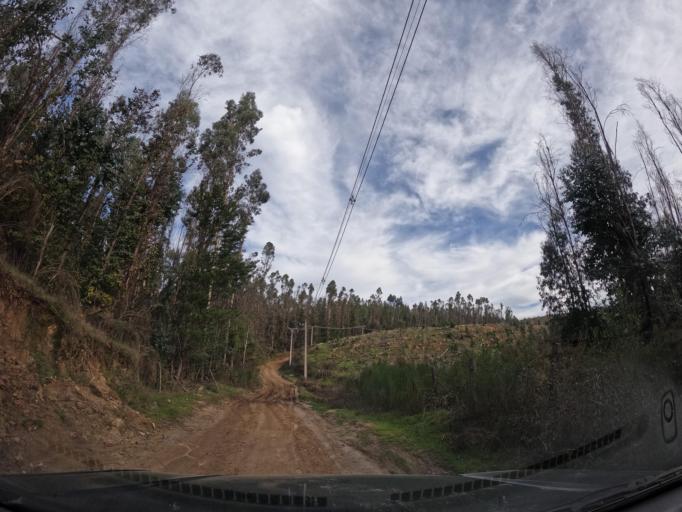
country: CL
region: Biobio
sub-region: Provincia de Concepcion
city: Chiguayante
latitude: -37.0199
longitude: -72.9144
